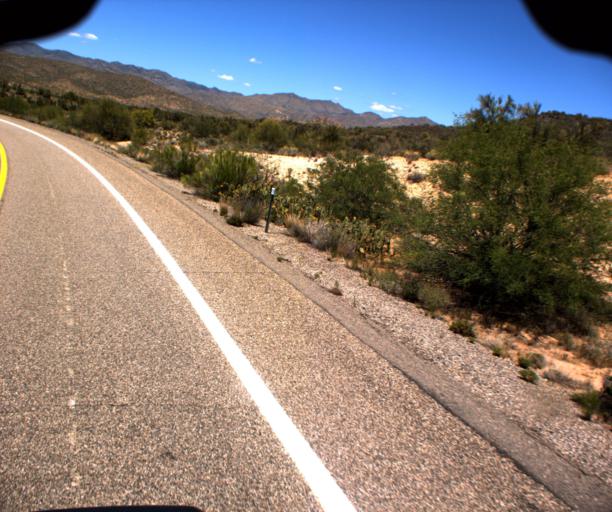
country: US
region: Arizona
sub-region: Yavapai County
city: Bagdad
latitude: 34.5156
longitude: -113.0754
